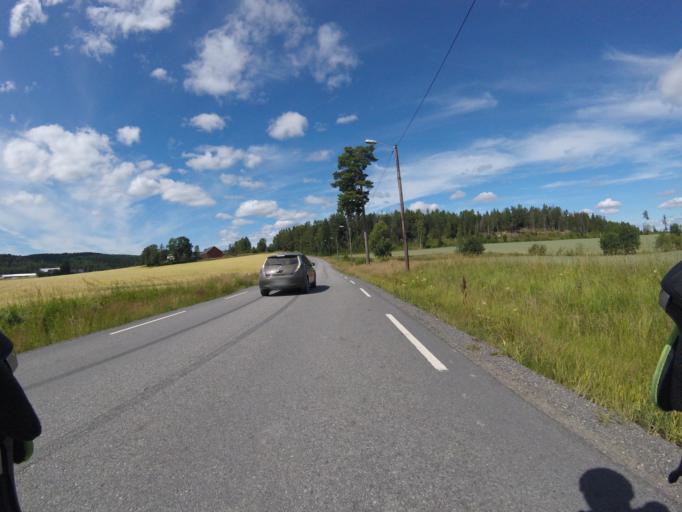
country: NO
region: Akershus
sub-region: Lorenskog
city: Kjenn
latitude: 59.9051
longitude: 10.9647
